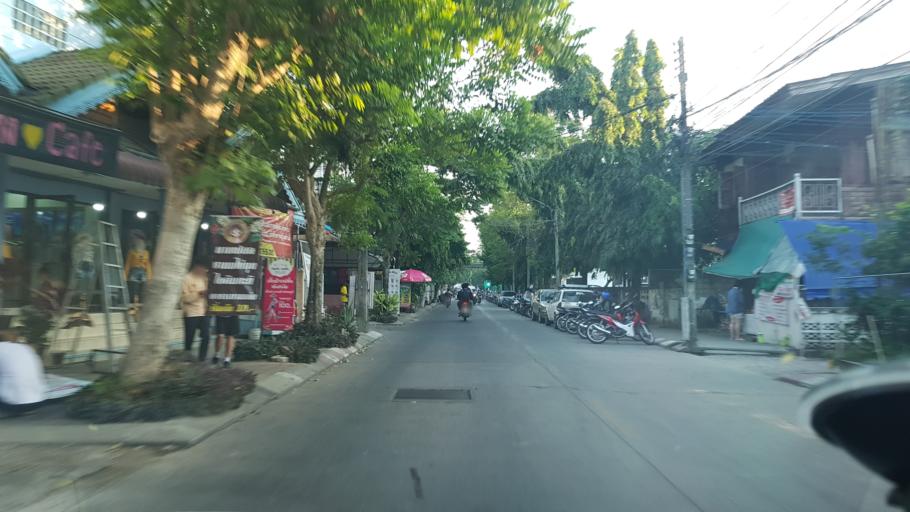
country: TH
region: Chiang Rai
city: Chiang Rai
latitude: 19.9101
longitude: 99.8350
